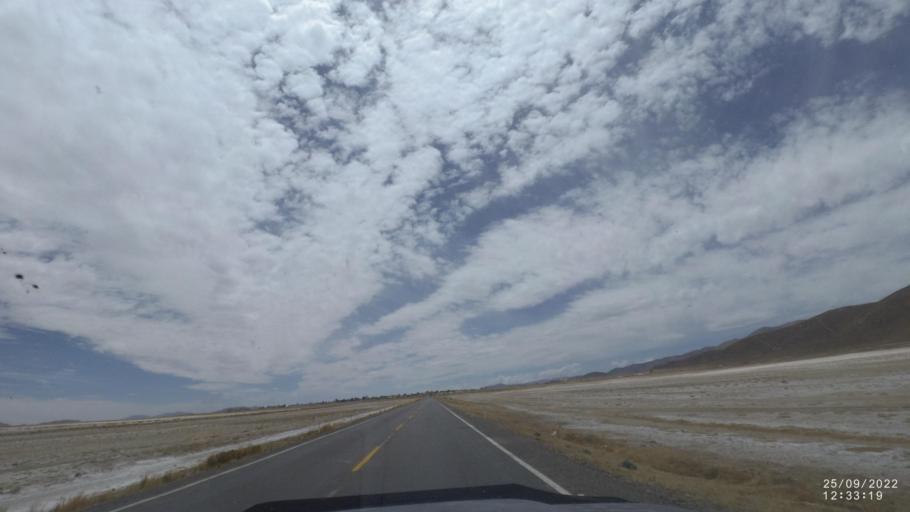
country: BO
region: Oruro
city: Machacamarca
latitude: -18.1955
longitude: -67.0129
